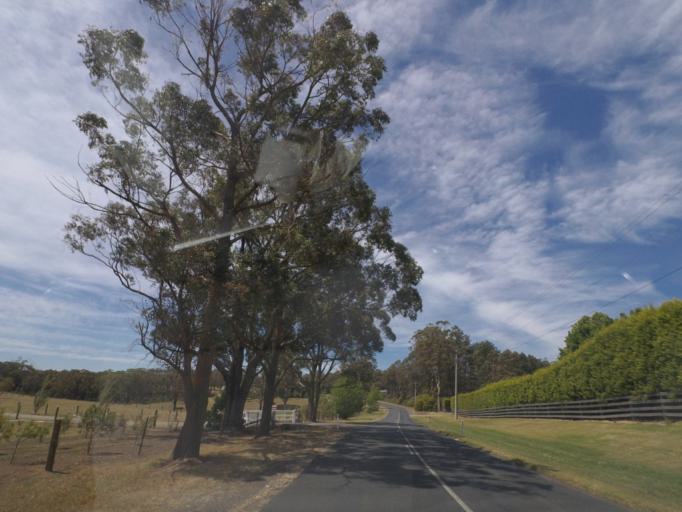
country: AU
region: New South Wales
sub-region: Wingecarribee
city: Colo Vale
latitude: -34.4080
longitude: 150.5266
